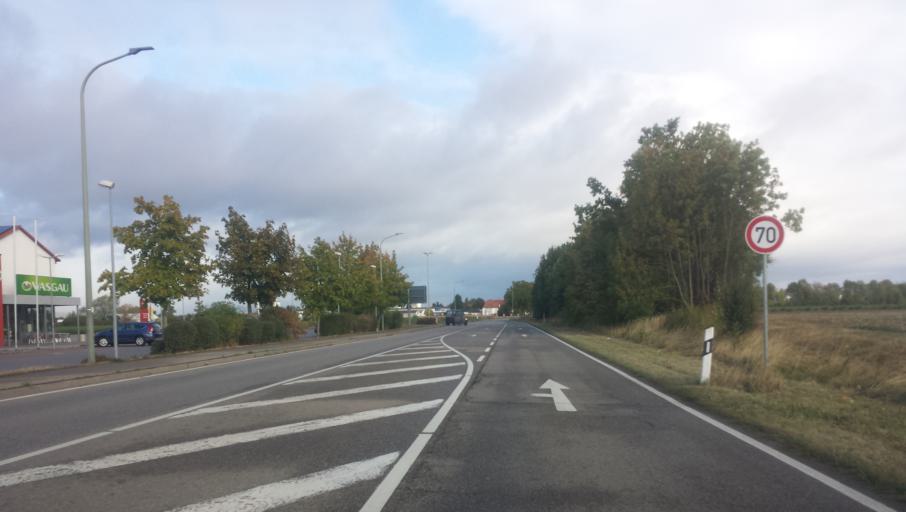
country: DE
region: Rheinland-Pfalz
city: Bohl-Iggelheim
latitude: 49.3737
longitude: 8.3075
